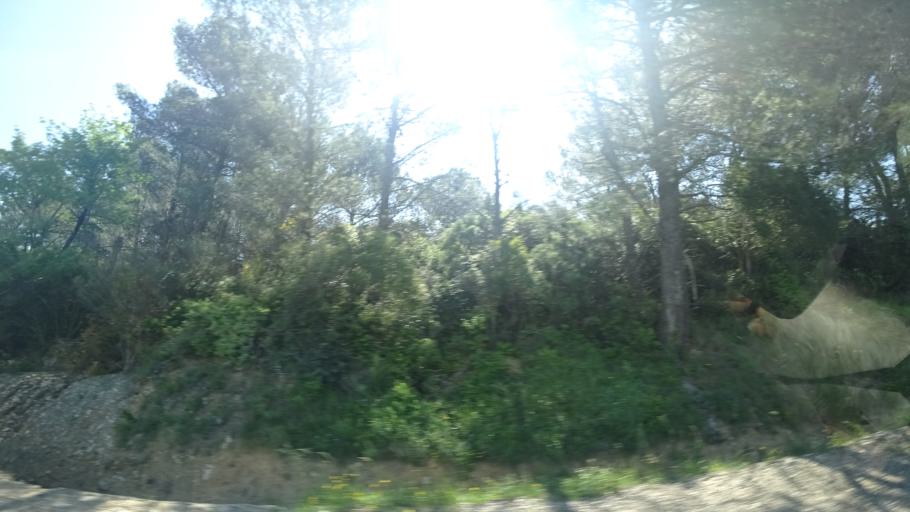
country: FR
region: Languedoc-Roussillon
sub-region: Departement de l'Herault
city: Olonzac
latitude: 43.3471
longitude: 2.7414
